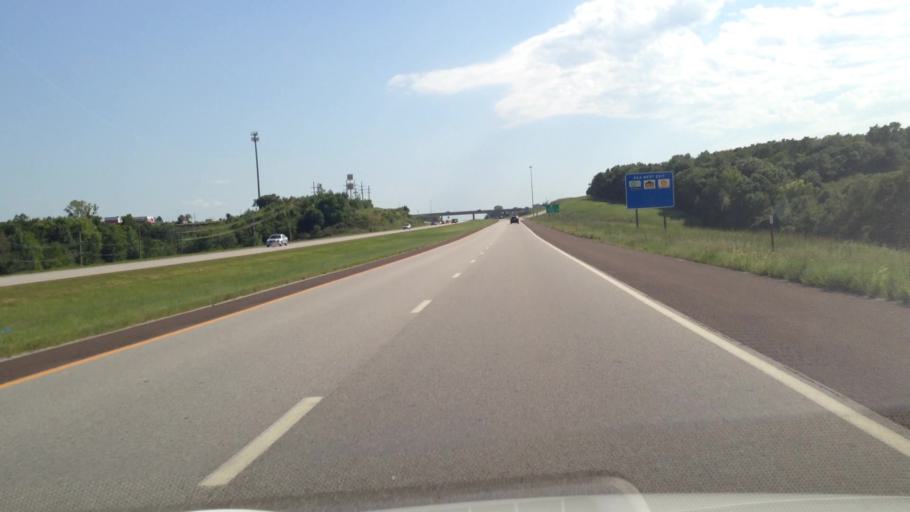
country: US
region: Kansas
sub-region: Miami County
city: Louisburg
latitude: 38.6287
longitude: -94.6948
